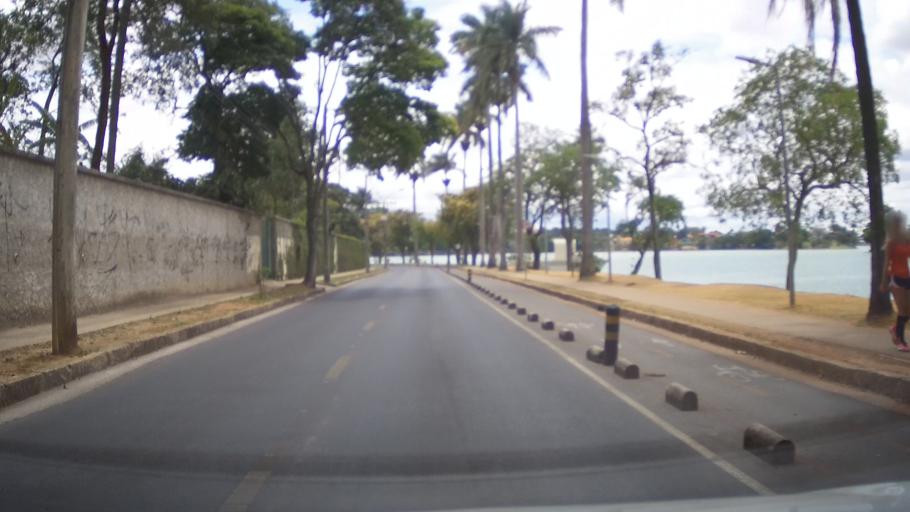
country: BR
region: Minas Gerais
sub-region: Belo Horizonte
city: Belo Horizonte
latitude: -19.8562
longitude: -43.9805
